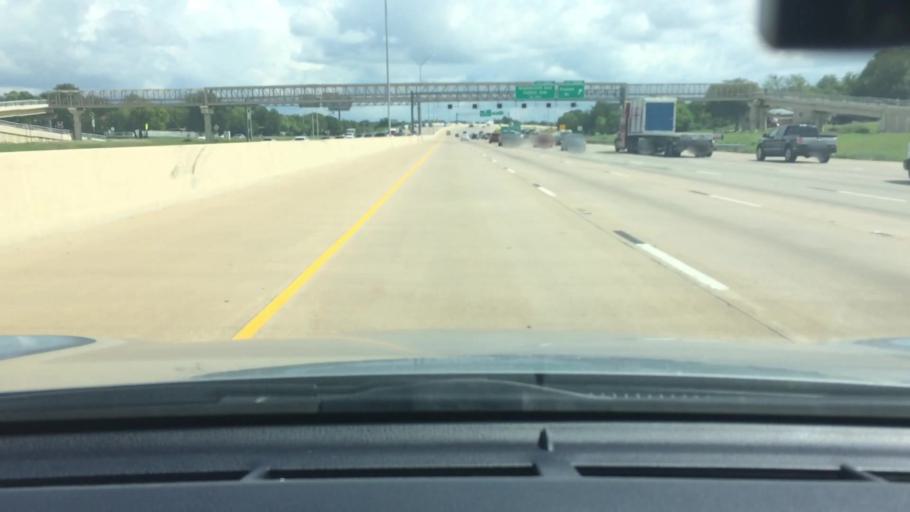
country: US
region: Texas
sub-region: Bexar County
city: Balcones Heights
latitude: 29.4786
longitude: -98.5217
